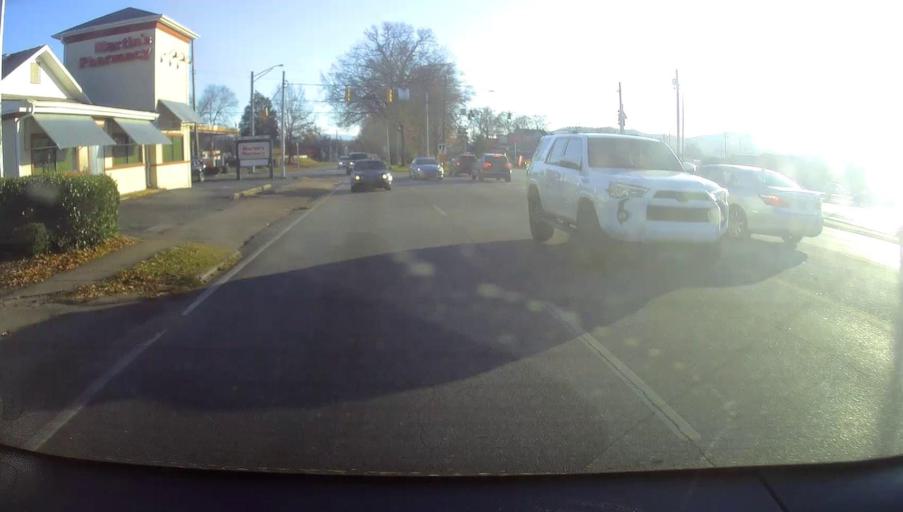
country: US
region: Alabama
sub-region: Calhoun County
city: Anniston
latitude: 33.6683
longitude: -85.8267
